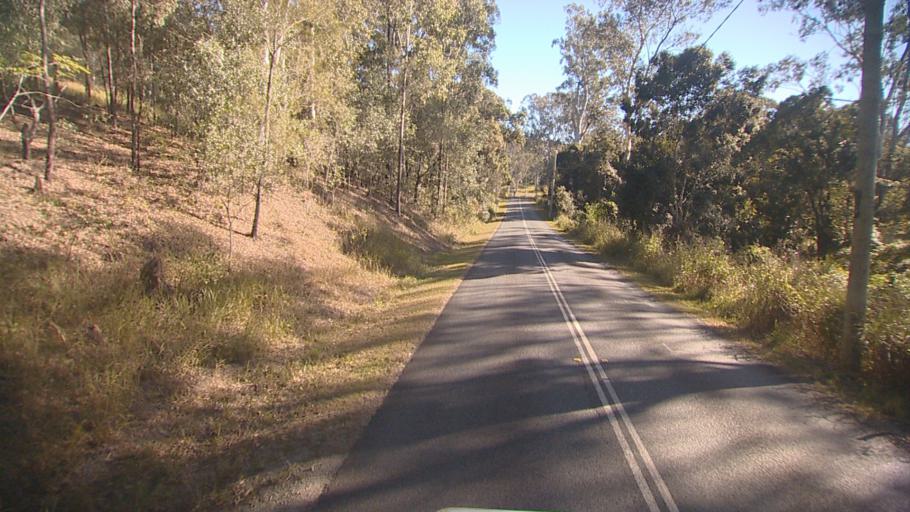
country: AU
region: Queensland
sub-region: Logan
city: Windaroo
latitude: -27.8055
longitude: 153.1697
